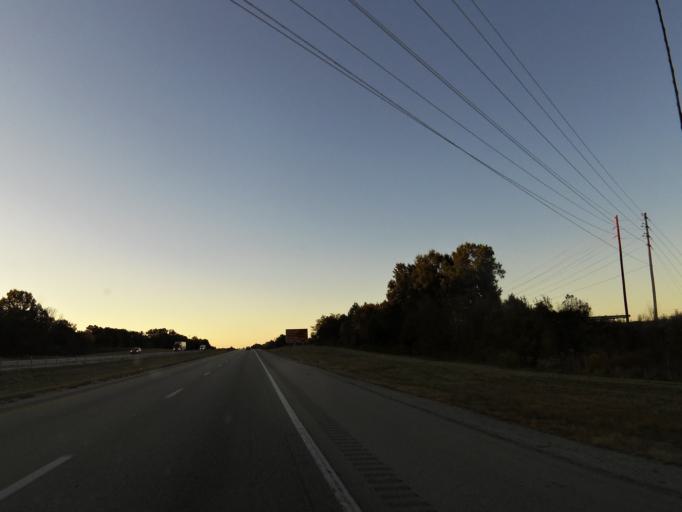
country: US
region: Kentucky
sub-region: Laurel County
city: London
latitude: 37.1736
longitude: -84.1286
